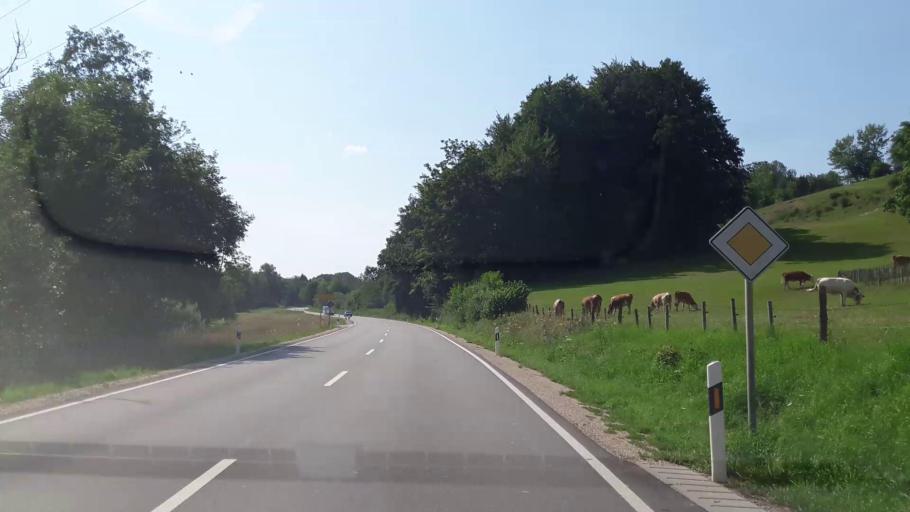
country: DE
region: Bavaria
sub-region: Upper Bavaria
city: Surberg
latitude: 47.8639
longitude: 12.7361
